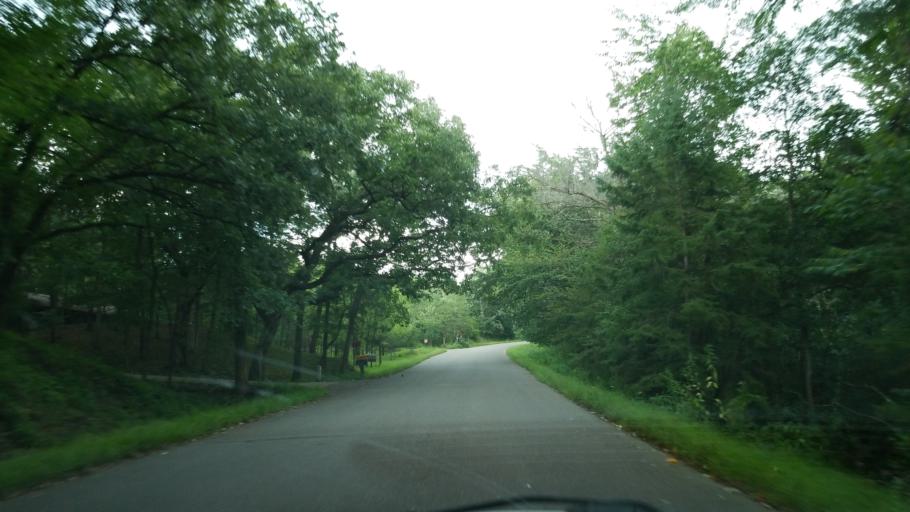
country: US
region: Minnesota
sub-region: Washington County
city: Afton
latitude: 44.8829
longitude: -92.7599
